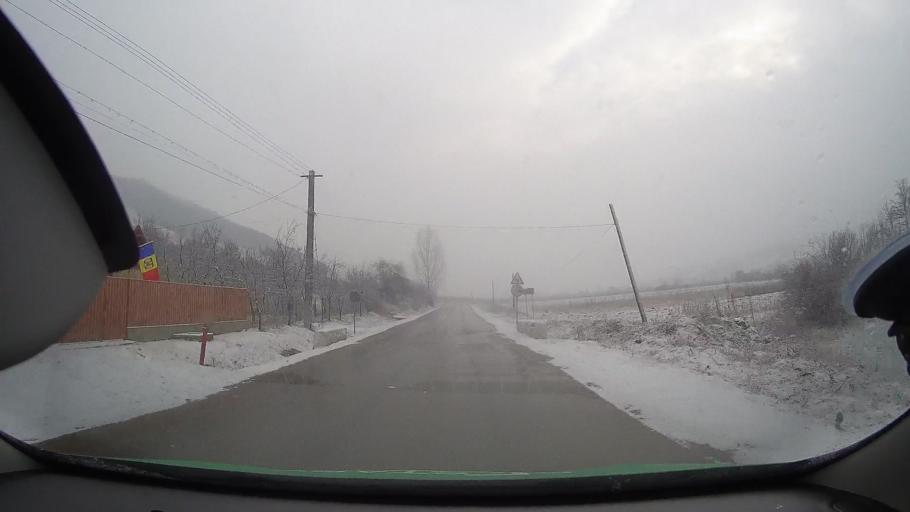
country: RO
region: Alba
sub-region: Comuna Lopadea Noua
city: Lopadea Noua
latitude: 46.3048
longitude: 23.8001
